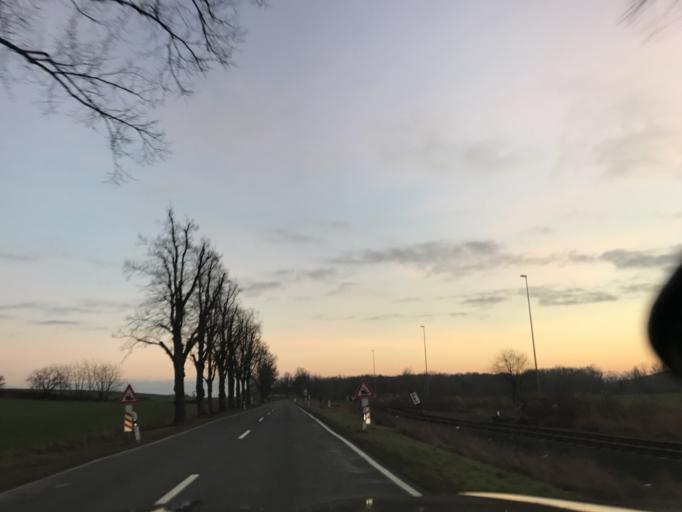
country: DE
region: Brandenburg
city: Ketzin
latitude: 52.5109
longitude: 12.8506
